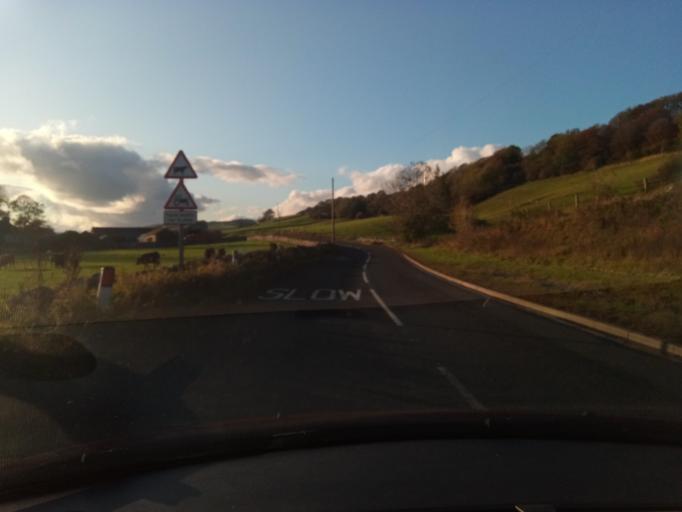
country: GB
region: England
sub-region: County Durham
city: Stanhope
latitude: 54.7456
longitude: -2.0511
